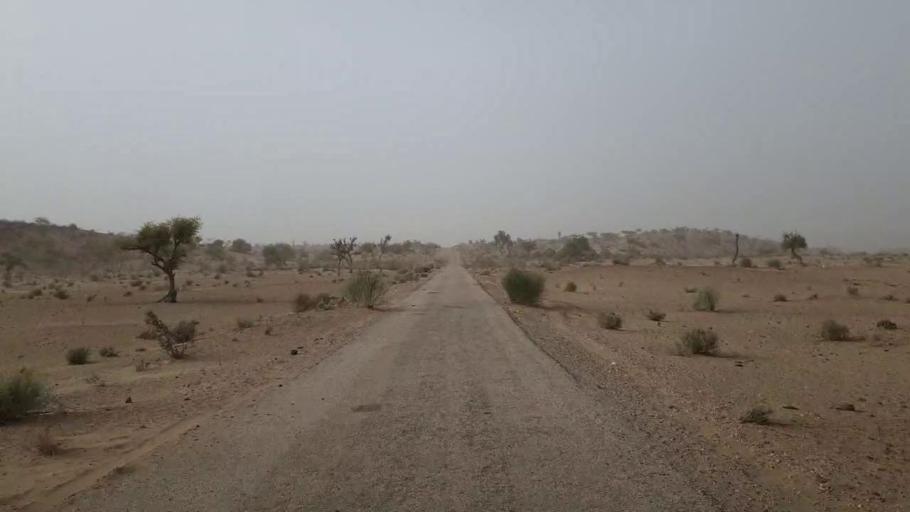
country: PK
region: Sindh
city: Islamkot
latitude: 24.5548
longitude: 70.3610
